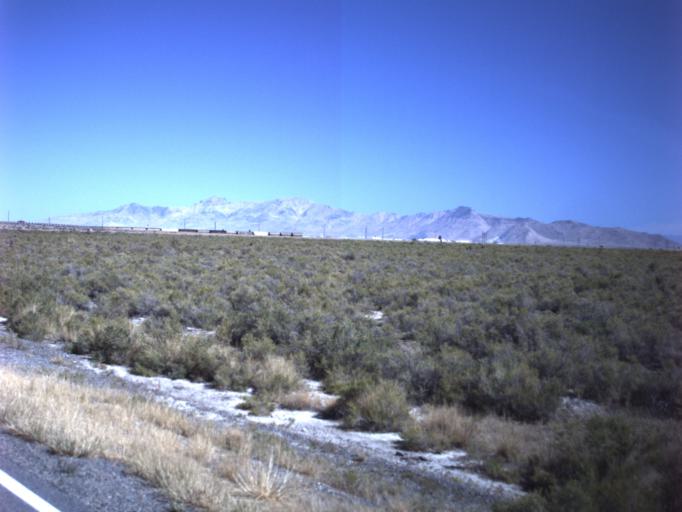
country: US
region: Utah
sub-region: Tooele County
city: Grantsville
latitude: 40.7410
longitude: -112.6544
